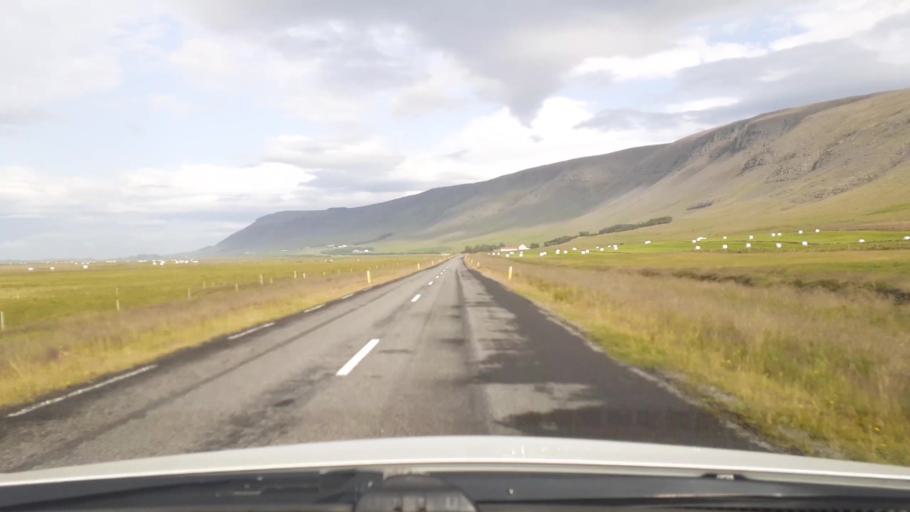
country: IS
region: Capital Region
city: Mosfellsbaer
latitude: 64.3286
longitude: -21.5084
